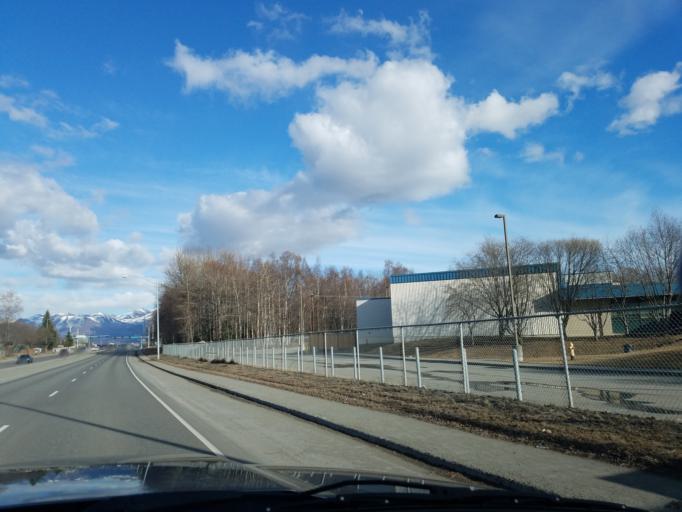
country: US
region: Alaska
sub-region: Anchorage Municipality
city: Anchorage
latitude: 61.1807
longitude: -149.9035
